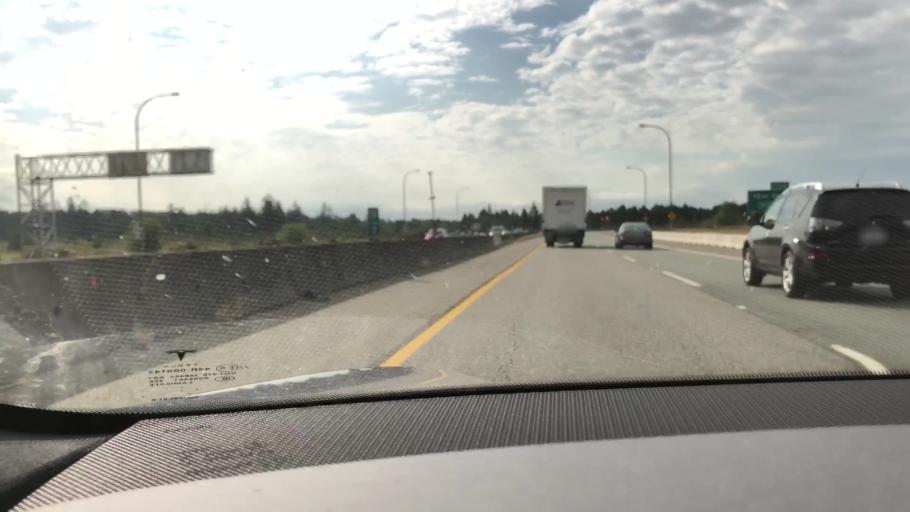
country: CA
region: British Columbia
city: Delta
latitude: 49.1436
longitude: -122.9362
